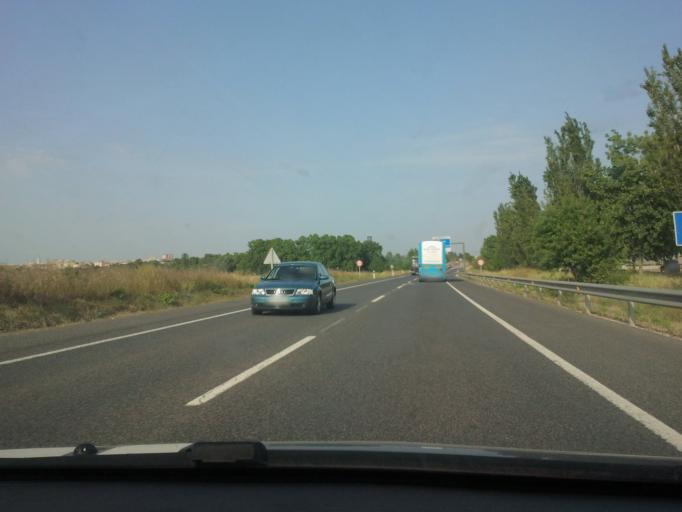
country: ES
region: Catalonia
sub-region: Provincia de Barcelona
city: Vilafranca del Penedes
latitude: 41.3342
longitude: 1.6752
